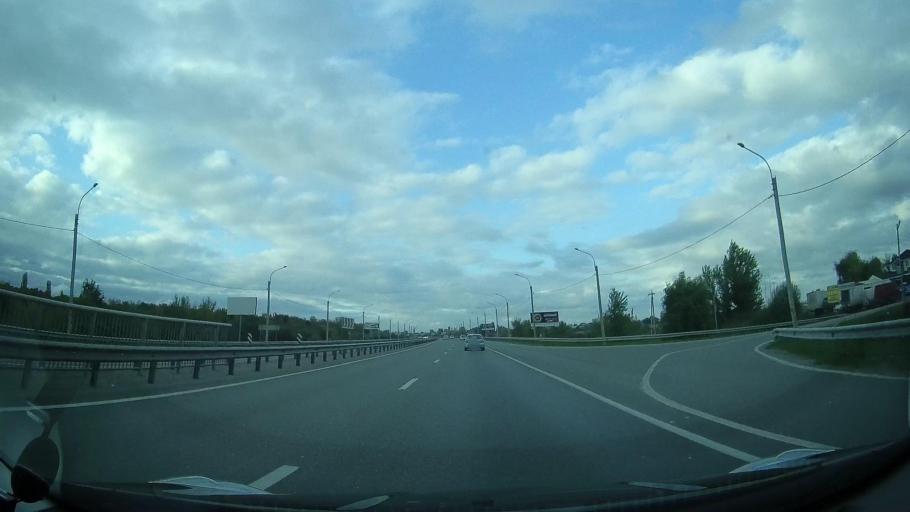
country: RU
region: Rostov
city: Bataysk
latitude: 47.1394
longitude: 39.7764
